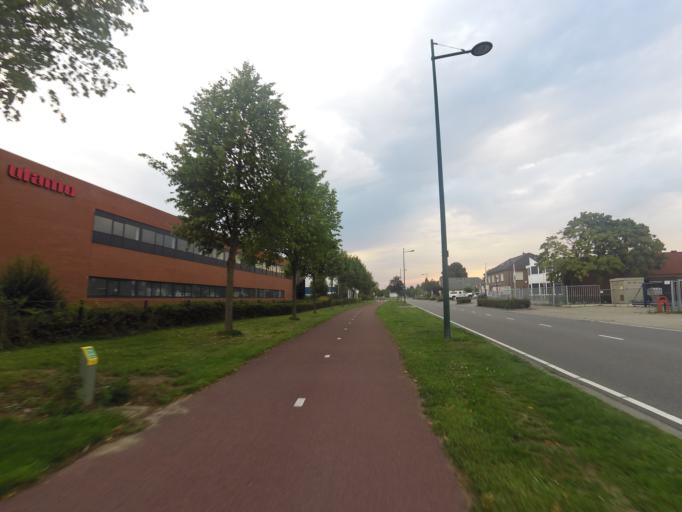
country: NL
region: Gelderland
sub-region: Oude IJsselstreek
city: Gendringen
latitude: 51.9039
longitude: 6.3668
